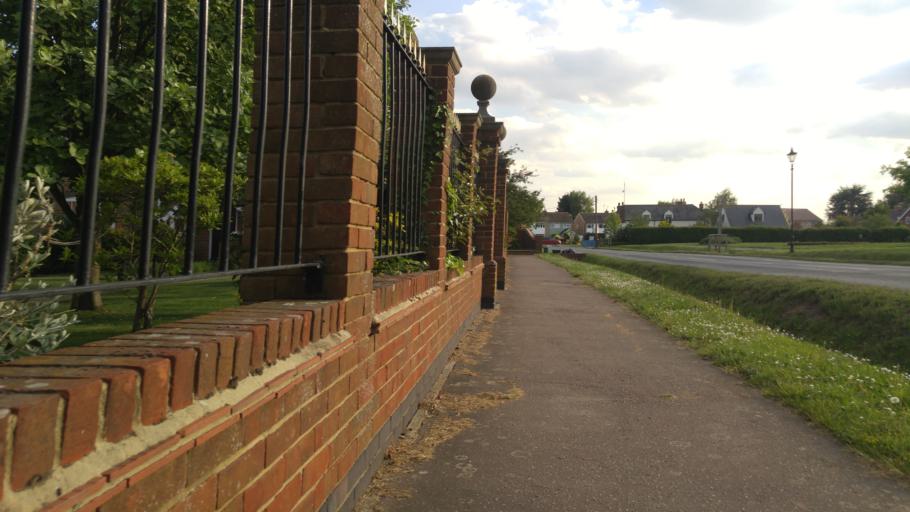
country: GB
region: England
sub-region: Essex
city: Eight Ash Green
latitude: 51.9238
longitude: 0.8047
